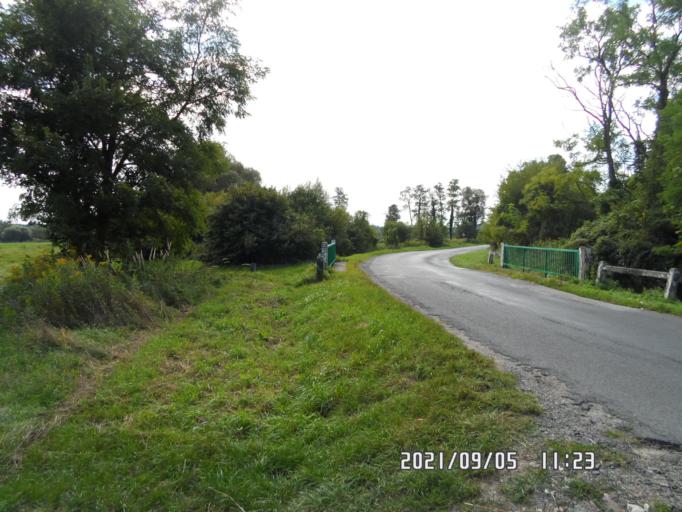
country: HU
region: Zala
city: Zalakomar
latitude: 46.4949
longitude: 17.2082
